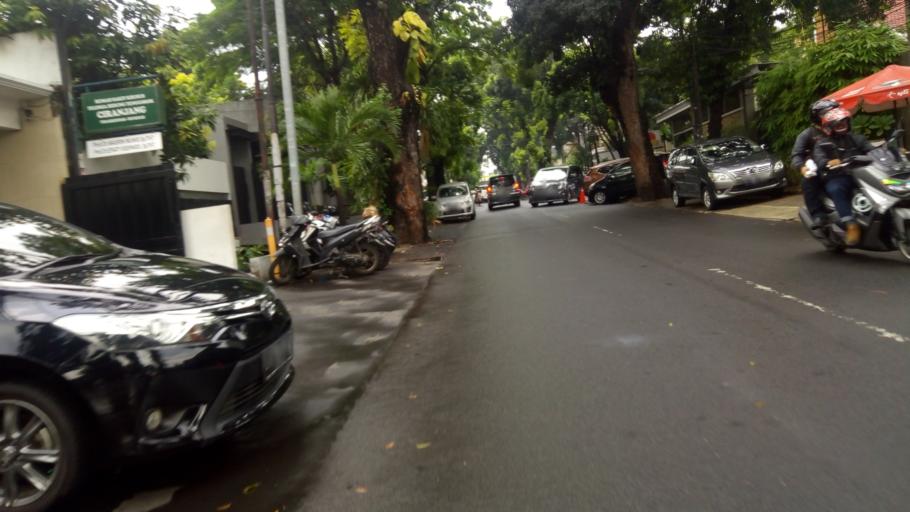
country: ID
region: Jakarta Raya
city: Jakarta
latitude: -6.2368
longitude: 106.8111
